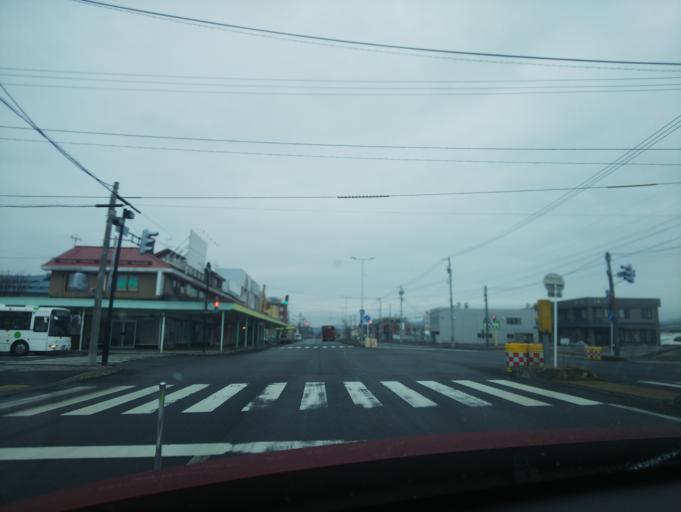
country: JP
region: Hokkaido
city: Nayoro
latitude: 44.3491
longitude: 142.4638
